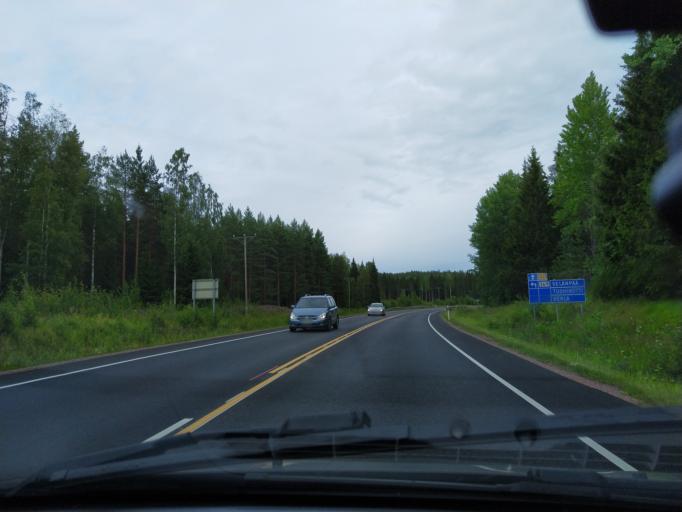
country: FI
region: Kymenlaakso
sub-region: Kouvola
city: Jaala
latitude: 61.0436
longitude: 26.5463
